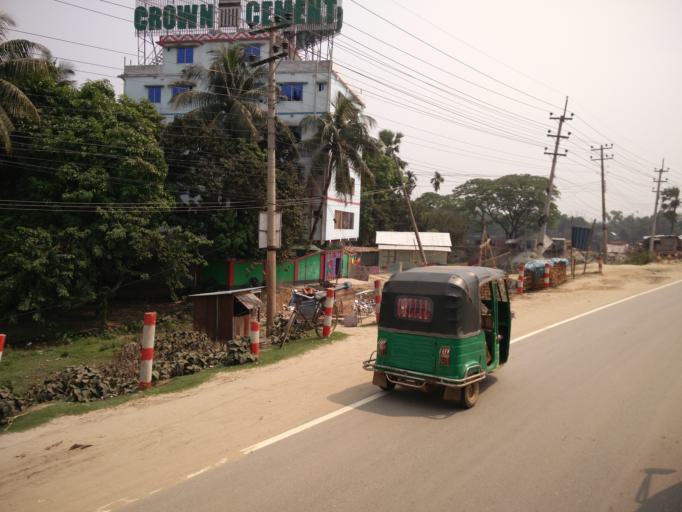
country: BD
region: Dhaka
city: Gafargaon
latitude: 24.4012
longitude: 90.3863
